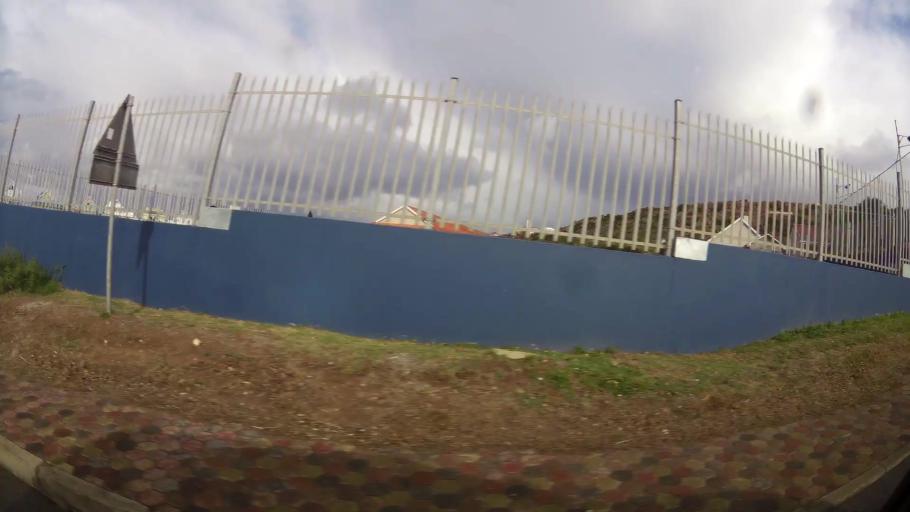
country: ZA
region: Western Cape
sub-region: Eden District Municipality
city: Mossel Bay
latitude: -34.1819
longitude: 22.1549
